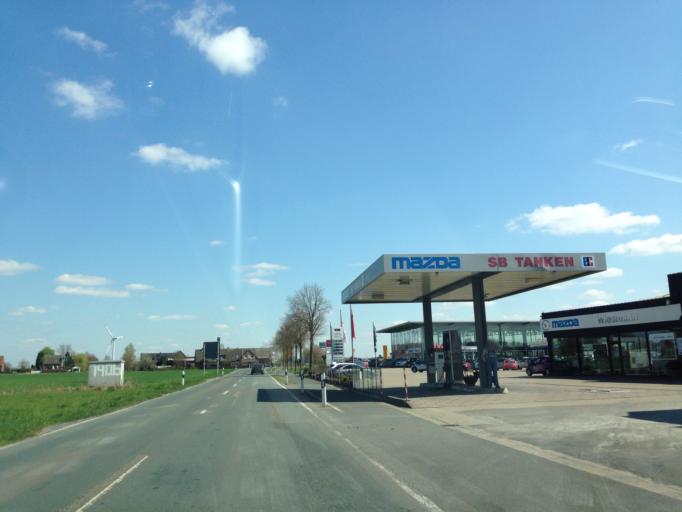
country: DE
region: North Rhine-Westphalia
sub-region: Regierungsbezirk Munster
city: Muenster
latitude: 51.8937
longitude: 7.5808
